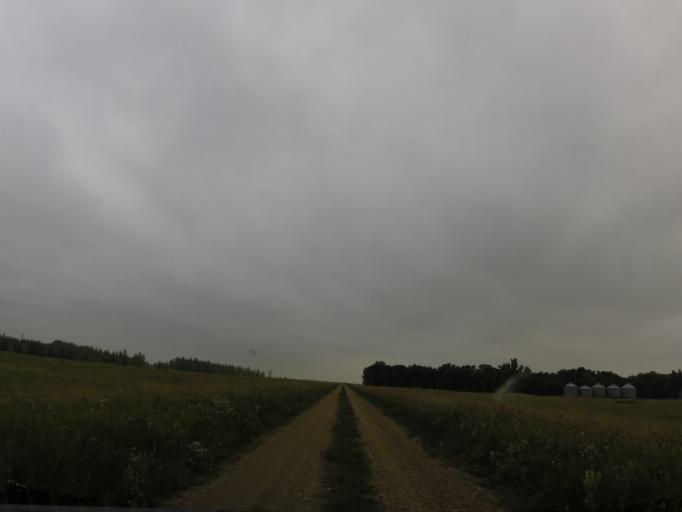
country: US
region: North Dakota
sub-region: Walsh County
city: Grafton
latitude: 48.4202
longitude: -97.1181
